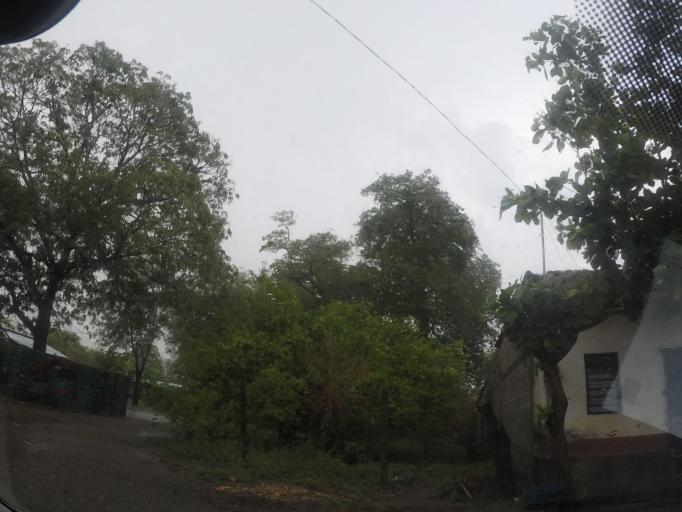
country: MX
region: Oaxaca
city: San Pedro Tapanatepec
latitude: 16.3639
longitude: -94.1957
